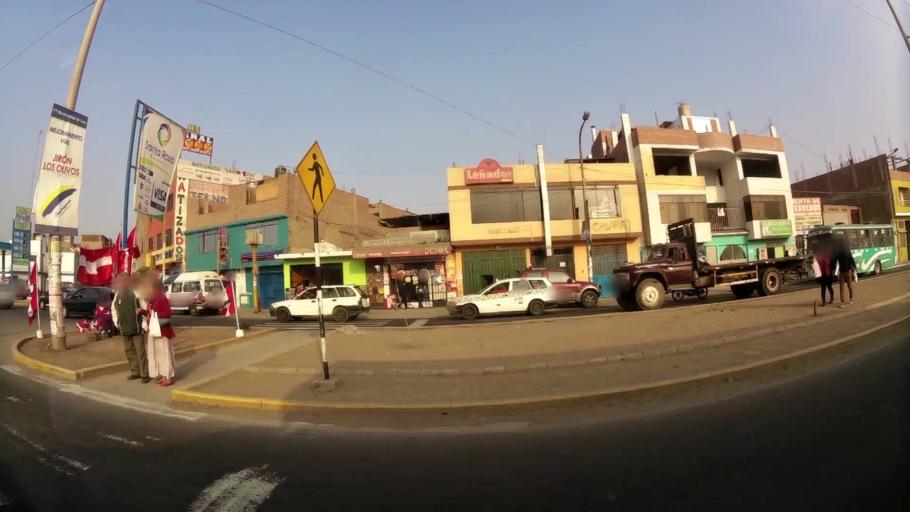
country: PE
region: Lima
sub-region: Lima
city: Independencia
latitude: -11.9840
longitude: -77.0996
